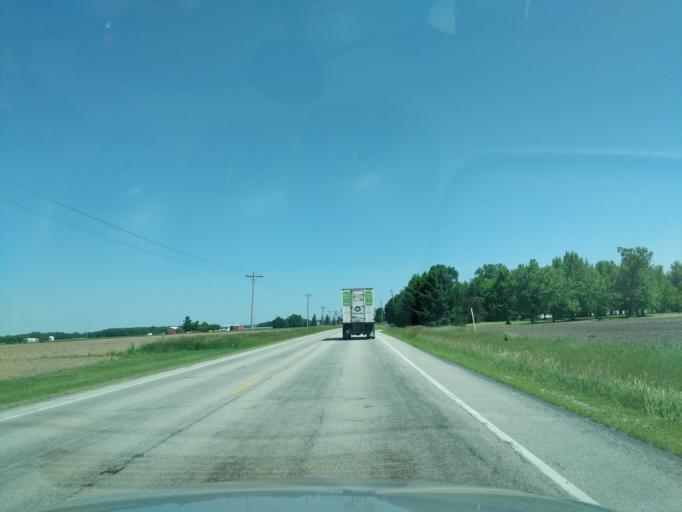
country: US
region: Indiana
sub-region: Whitley County
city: Columbia City
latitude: 41.0444
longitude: -85.4706
